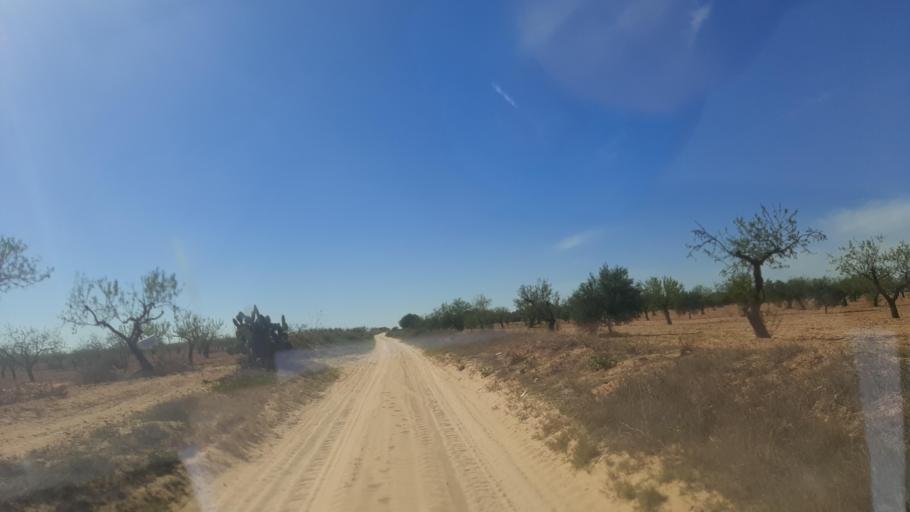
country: TN
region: Safaqis
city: Sfax
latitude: 34.8200
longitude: 10.5514
